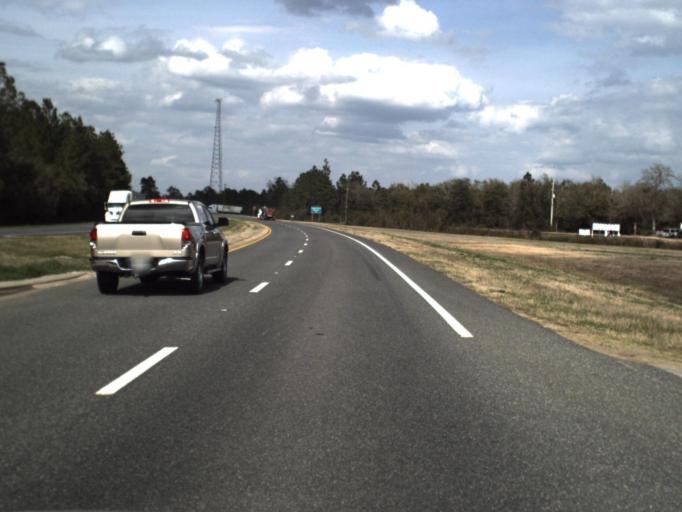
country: US
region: Florida
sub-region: Bay County
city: Youngstown
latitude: 30.5310
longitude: -85.3966
